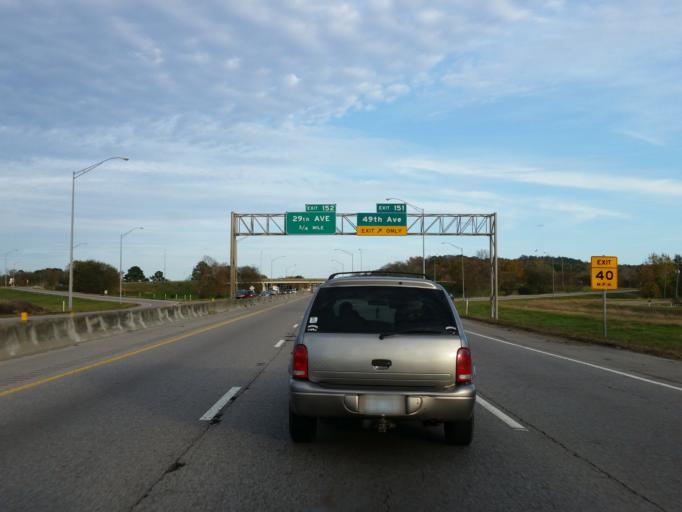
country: US
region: Mississippi
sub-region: Lauderdale County
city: Meridian
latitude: 32.3490
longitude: -88.7309
